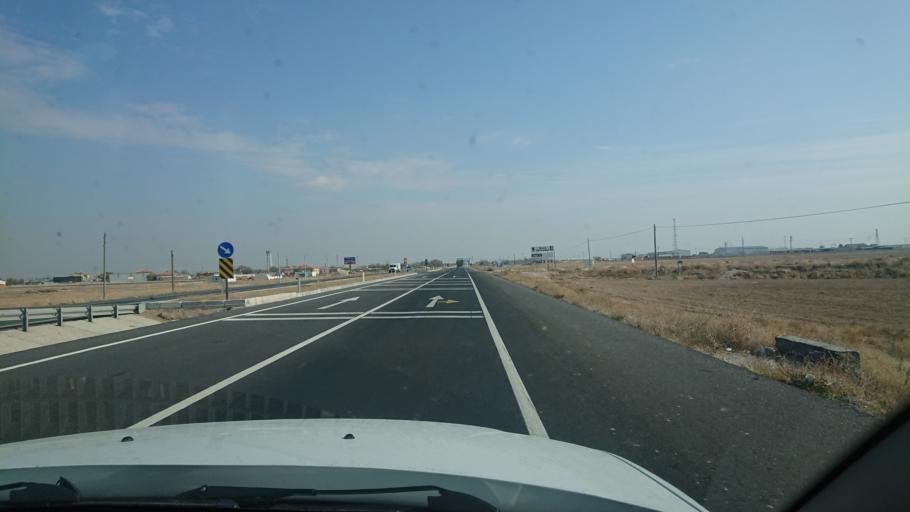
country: TR
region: Aksaray
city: Yesilova
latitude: 38.3224
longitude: 33.8730
